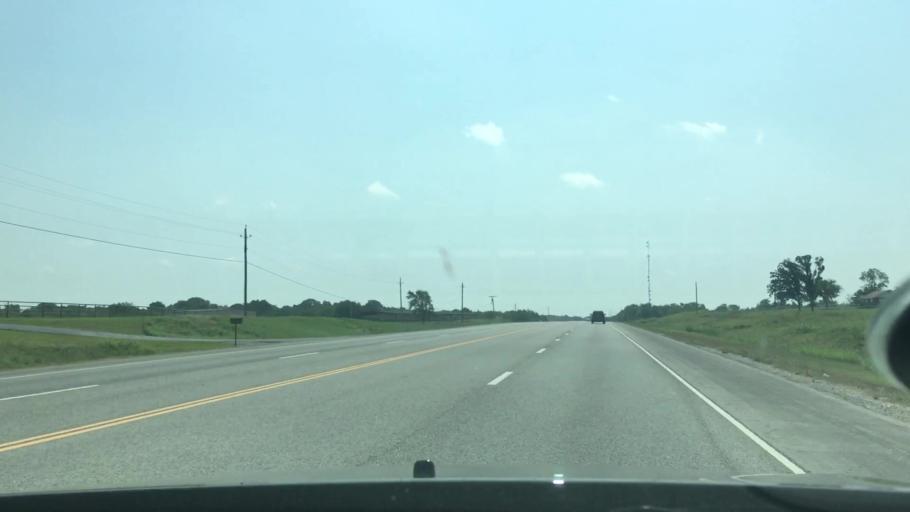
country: US
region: Oklahoma
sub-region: Atoka County
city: Atoka
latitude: 34.3647
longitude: -96.1001
